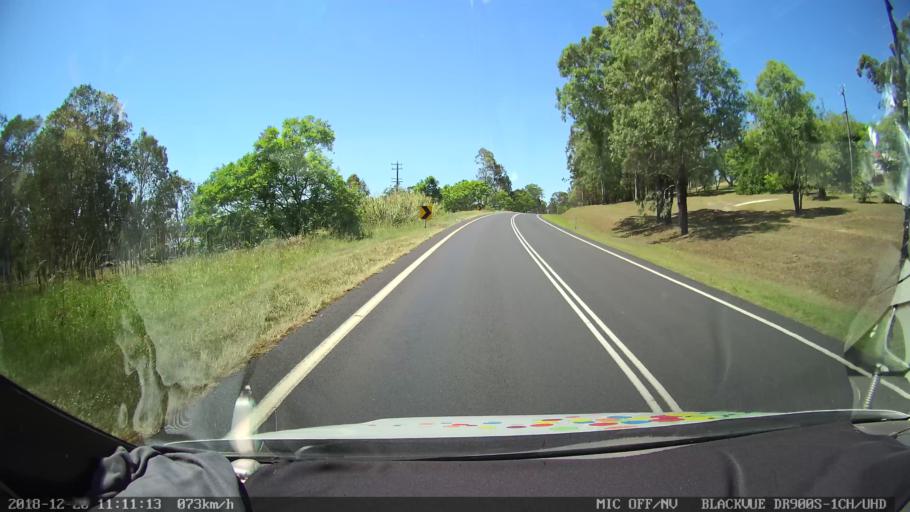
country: AU
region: New South Wales
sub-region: Richmond Valley
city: Casino
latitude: -28.9586
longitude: 153.0134
